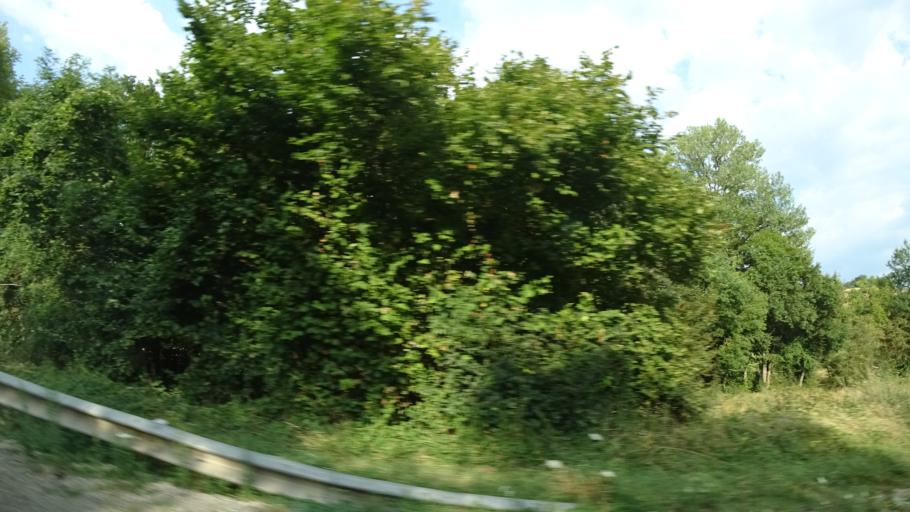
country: FR
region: Midi-Pyrenees
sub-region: Departement de l'Aveyron
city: Saint-Christophe-Vallon
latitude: 44.4929
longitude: 2.3879
